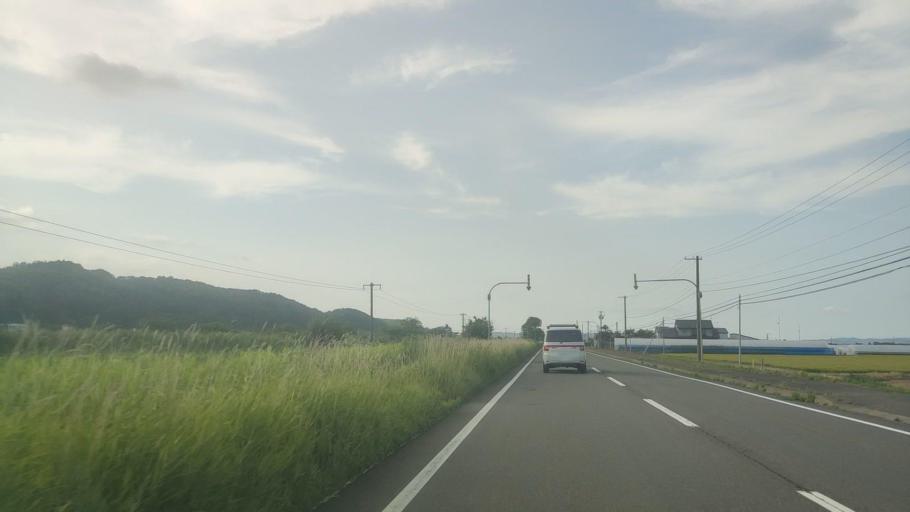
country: JP
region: Hokkaido
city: Iwamizawa
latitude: 42.9929
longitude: 141.7906
